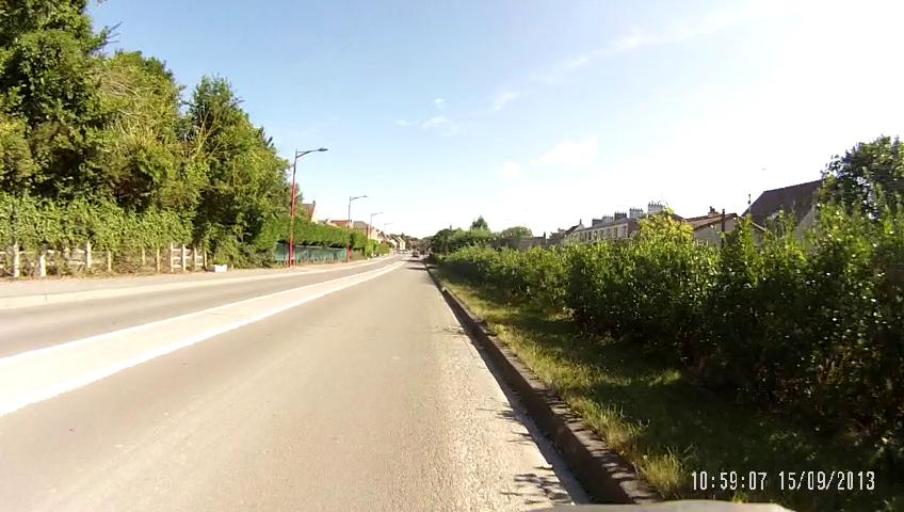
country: FR
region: Nord-Pas-de-Calais
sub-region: Departement du Nord
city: Zuydcoote
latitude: 51.0634
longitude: 2.4884
